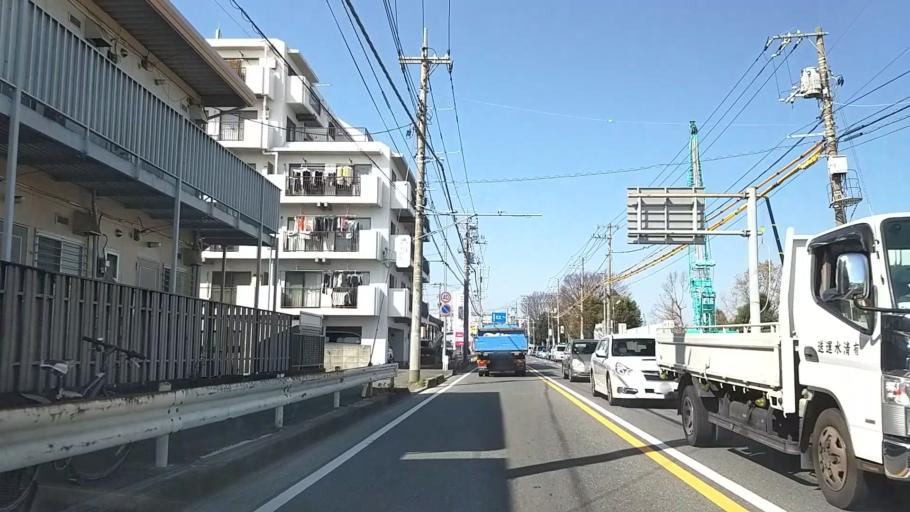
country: JP
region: Kanagawa
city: Kamakura
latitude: 35.3619
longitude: 139.5406
